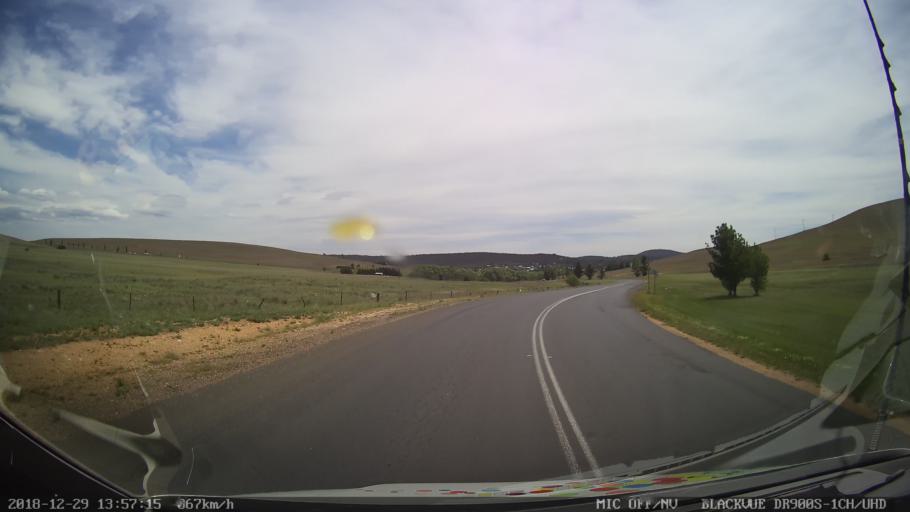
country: AU
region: New South Wales
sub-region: Cooma-Monaro
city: Cooma
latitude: -36.2391
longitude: 149.1439
